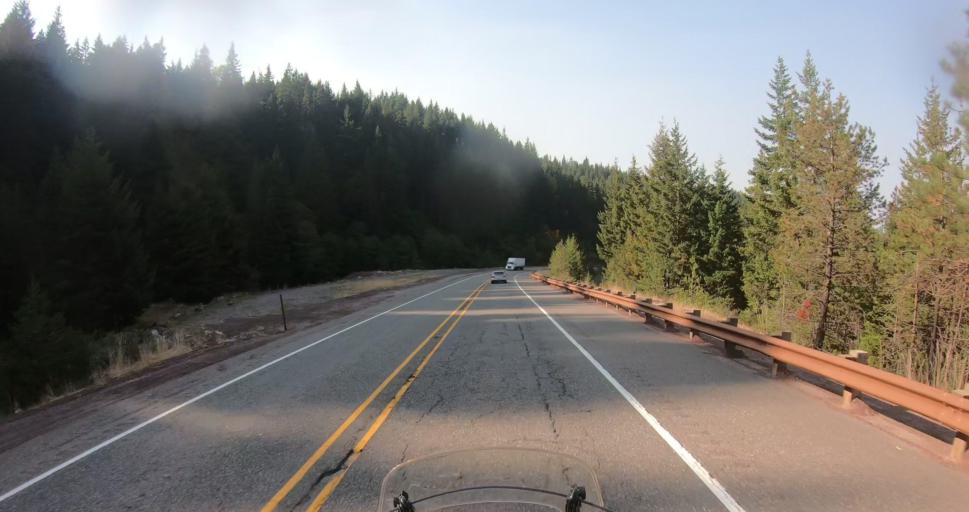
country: US
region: Oregon
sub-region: Hood River County
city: Odell
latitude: 45.4230
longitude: -121.5718
